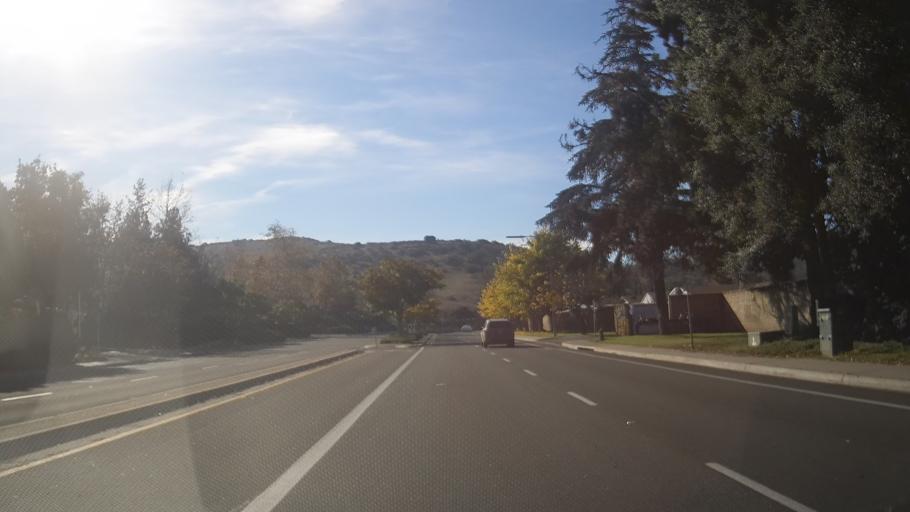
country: US
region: California
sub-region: San Diego County
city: Poway
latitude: 32.9531
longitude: -117.0409
